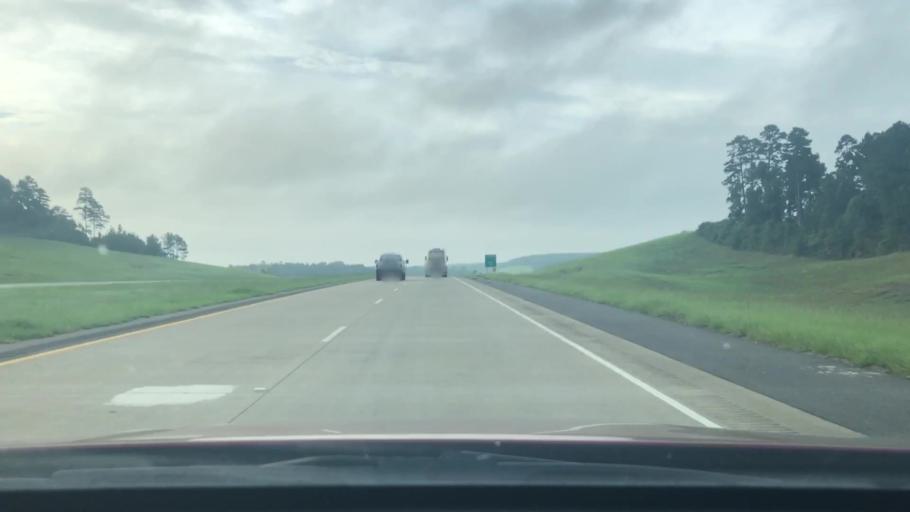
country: US
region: Louisiana
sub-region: Caddo Parish
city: Vivian
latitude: 32.9499
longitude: -93.8995
